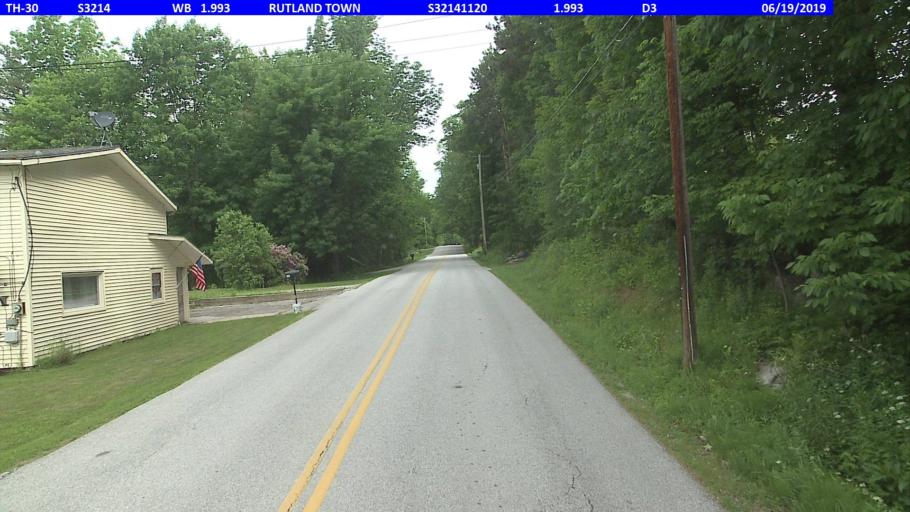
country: US
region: Vermont
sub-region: Rutland County
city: Rutland
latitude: 43.6365
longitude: -72.9437
